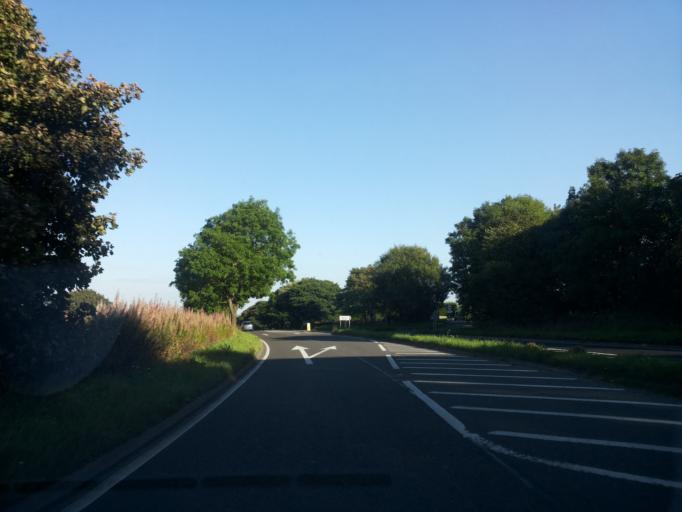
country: GB
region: England
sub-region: Derbyshire
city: Tideswell
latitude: 53.2387
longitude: -1.7975
